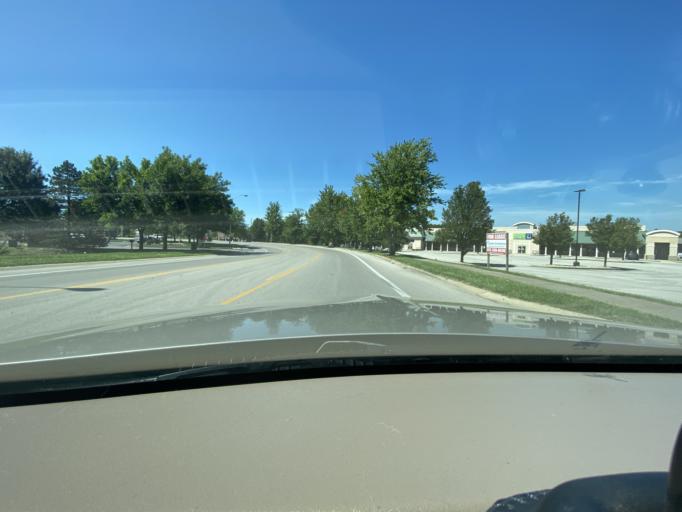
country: US
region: Indiana
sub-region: Monroe County
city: Bloomington
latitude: 39.1464
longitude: -86.5775
